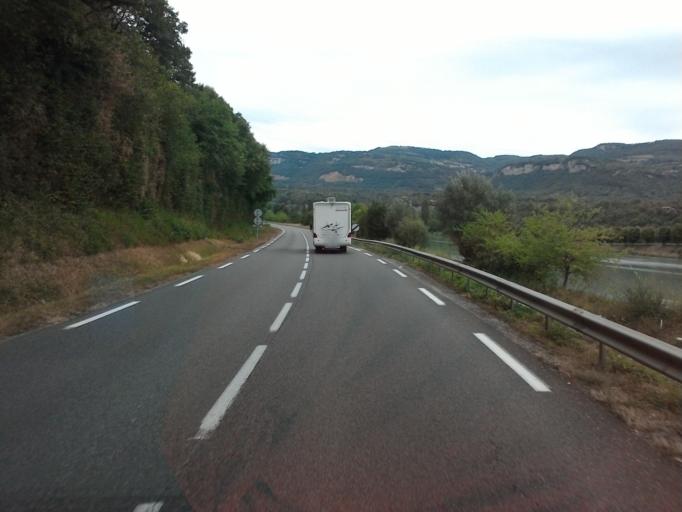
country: FR
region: Rhone-Alpes
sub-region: Departement de l'Ain
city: Sault-Brenaz
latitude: 45.8436
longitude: 5.4155
